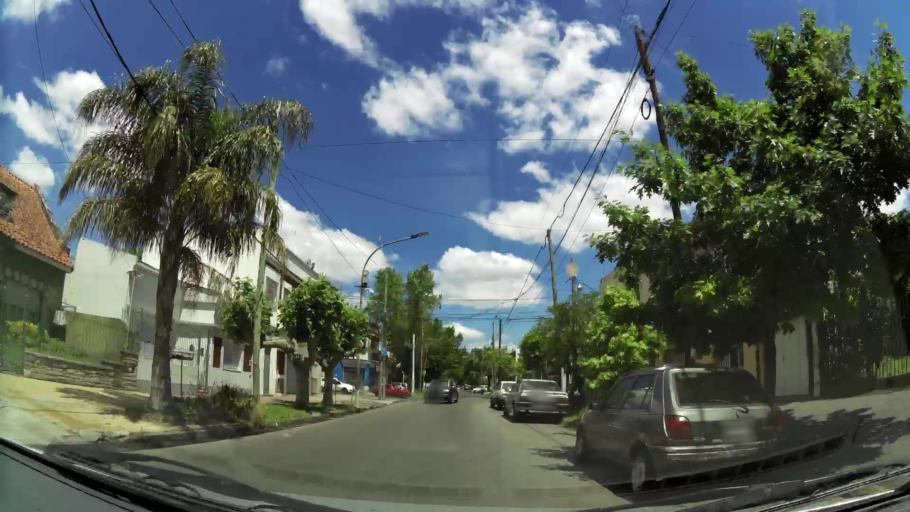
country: AR
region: Buenos Aires
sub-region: Partido de Lomas de Zamora
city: Lomas de Zamora
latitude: -34.7329
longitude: -58.4028
